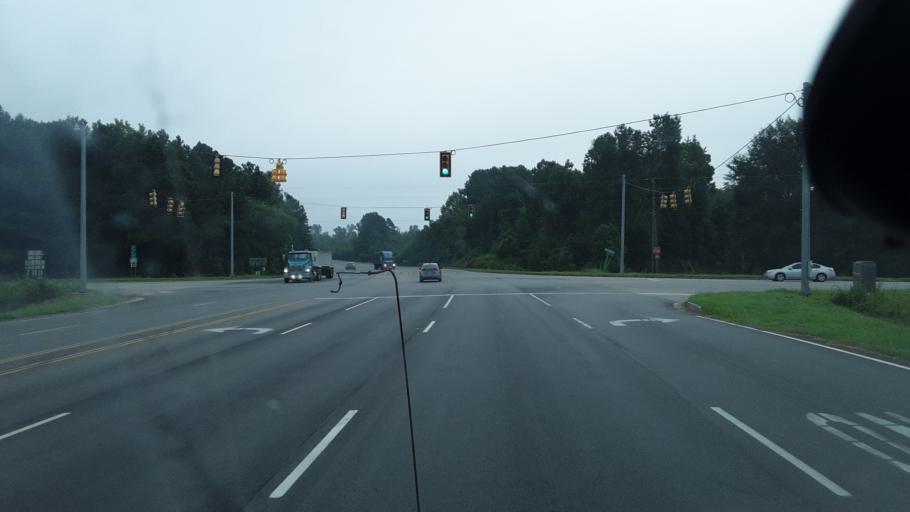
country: US
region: South Carolina
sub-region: Florence County
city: Johnsonville
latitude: 33.8824
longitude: -79.4534
